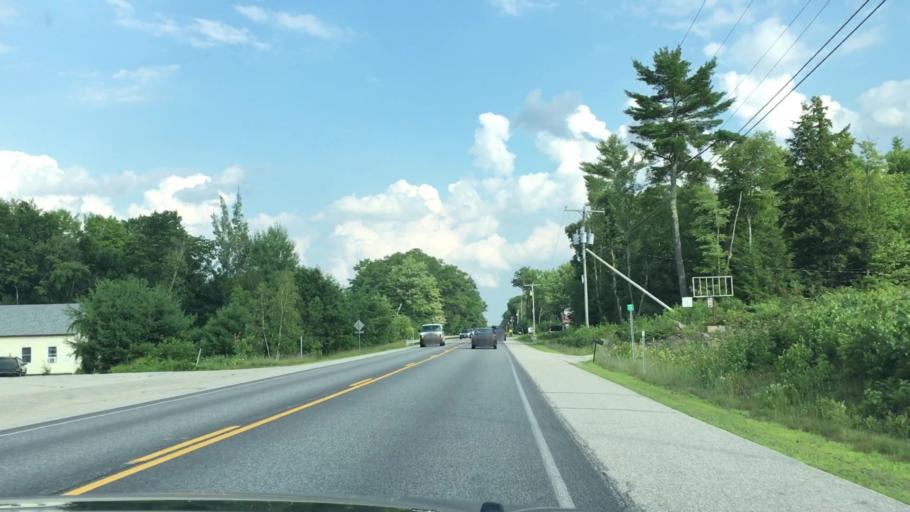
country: US
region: New Hampshire
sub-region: Strafford County
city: Farmington
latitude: 43.3989
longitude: -71.1056
